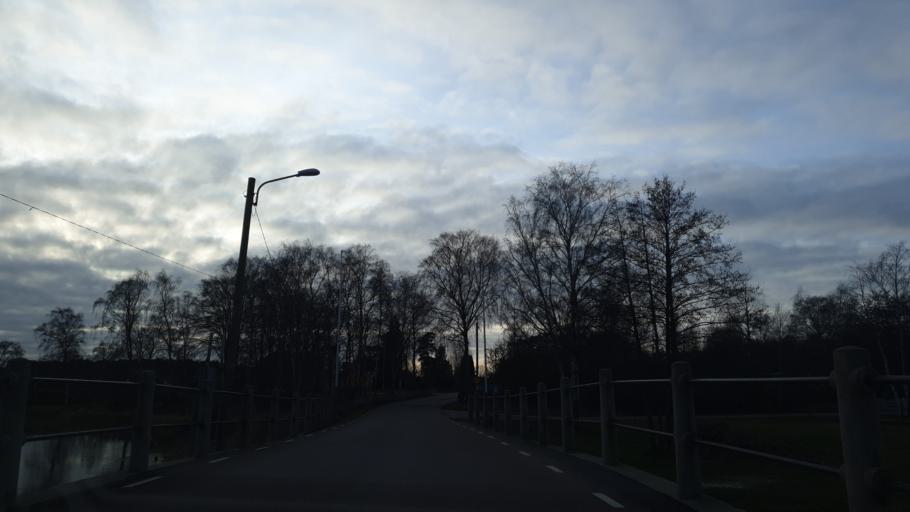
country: SE
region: Kalmar
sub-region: Torsas Kommun
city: Torsas
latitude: 56.2577
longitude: 16.0394
